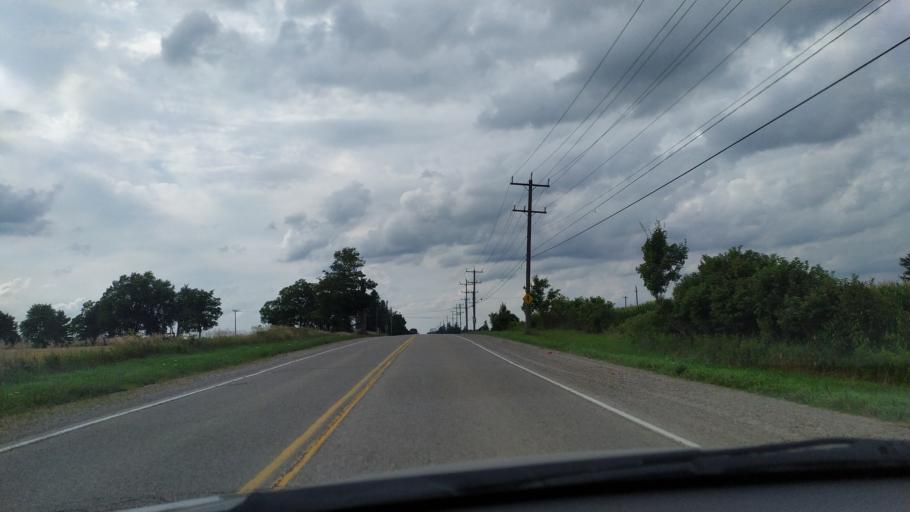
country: CA
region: Ontario
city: Kitchener
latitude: 43.3588
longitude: -80.5460
